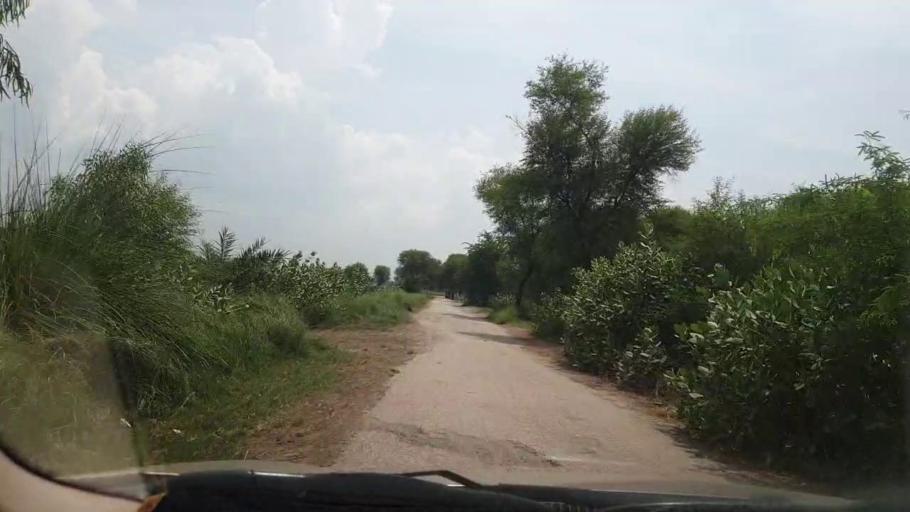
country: PK
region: Sindh
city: Larkana
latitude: 27.5976
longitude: 68.1238
